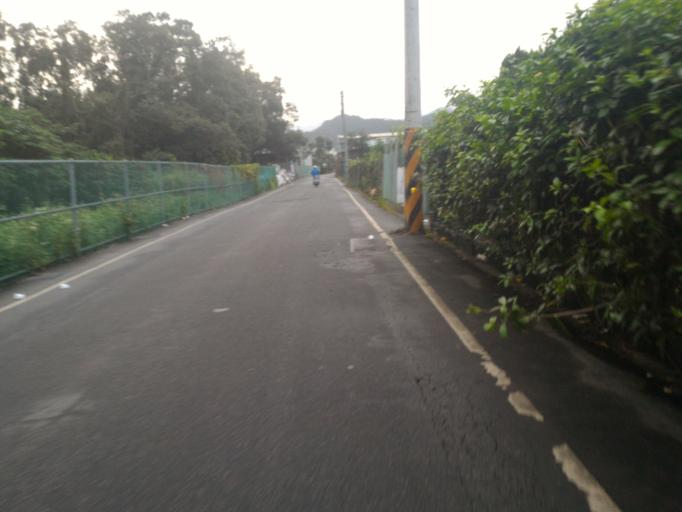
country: TW
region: Taipei
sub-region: Taipei
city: Banqiao
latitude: 24.9590
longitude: 121.4028
